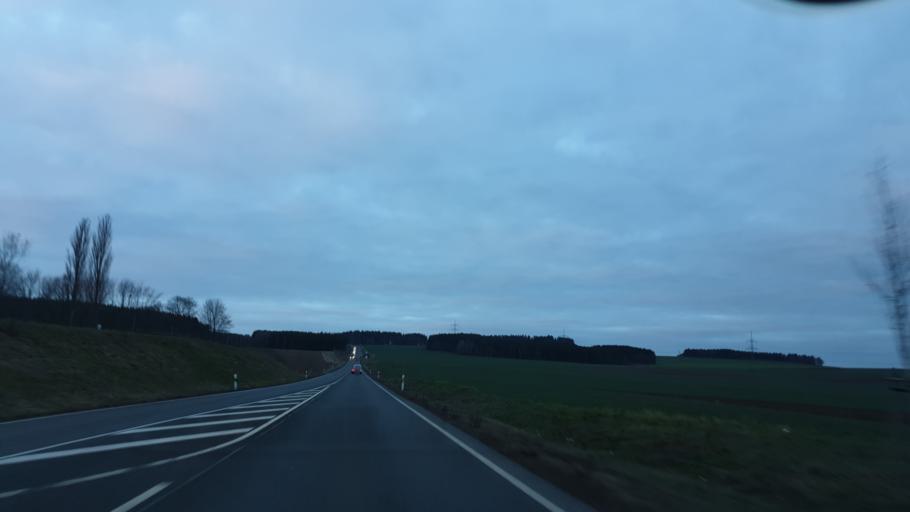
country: DE
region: Saxony
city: Dorfchemnitz
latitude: 50.6592
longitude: 12.8094
